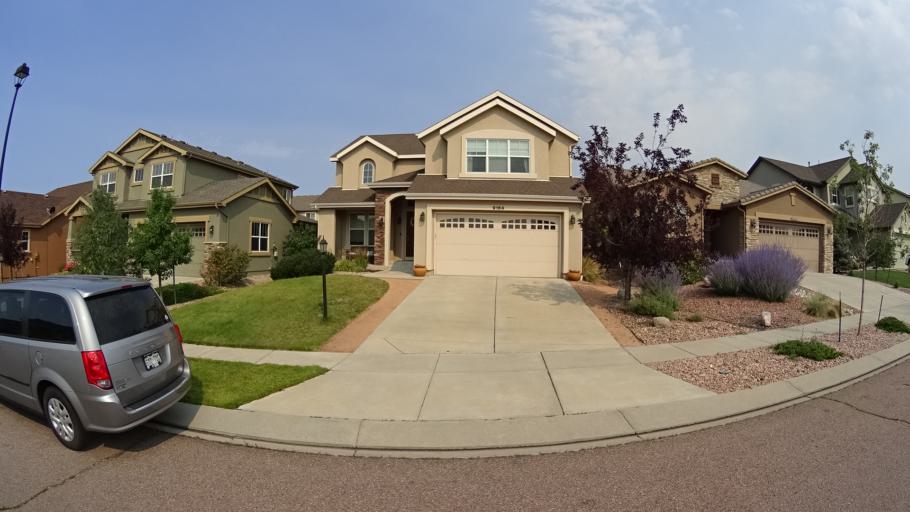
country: US
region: Colorado
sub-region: El Paso County
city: Black Forest
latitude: 38.9646
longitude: -104.7321
